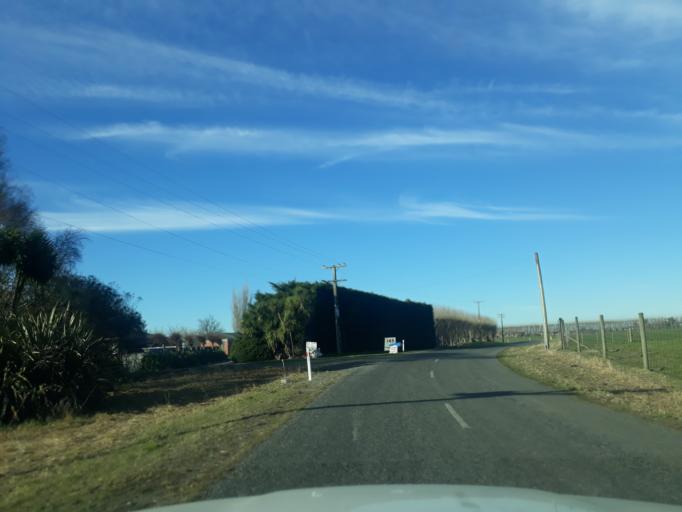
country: NZ
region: Canterbury
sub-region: Timaru District
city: Timaru
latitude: -44.2695
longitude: 171.3403
